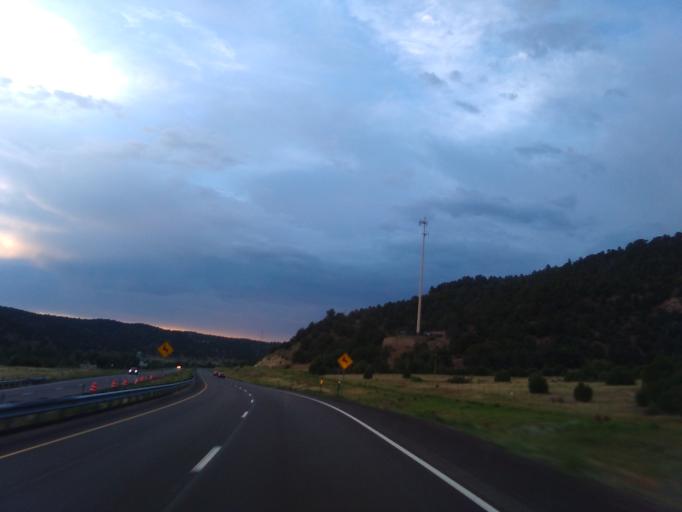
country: US
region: Colorado
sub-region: Las Animas County
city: Trinidad
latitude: 37.0963
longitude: -104.5193
